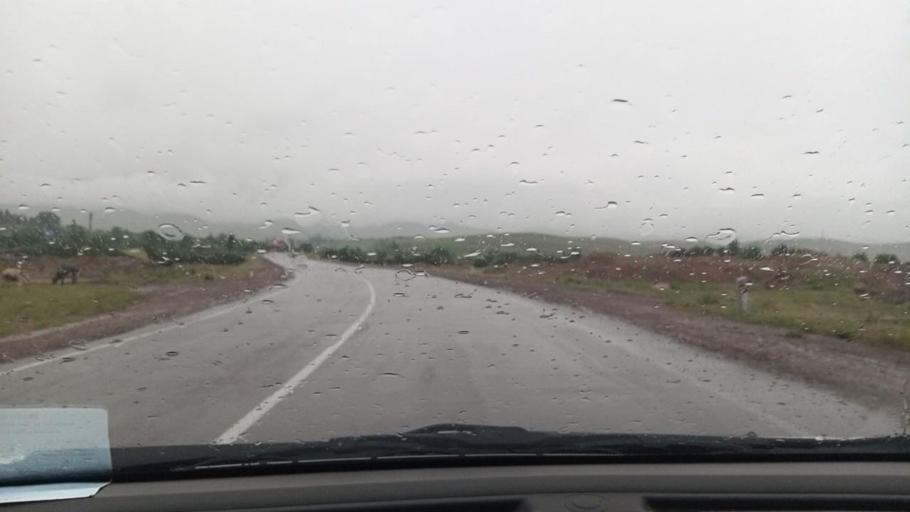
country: UZ
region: Toshkent
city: Angren
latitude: 41.0462
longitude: 70.1585
